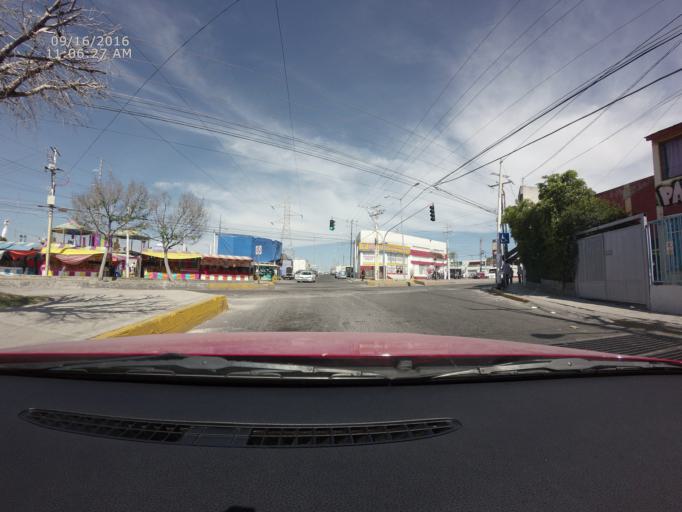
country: MX
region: Queretaro
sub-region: Queretaro
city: Sergio Villasenor
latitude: 20.6284
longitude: -100.4063
